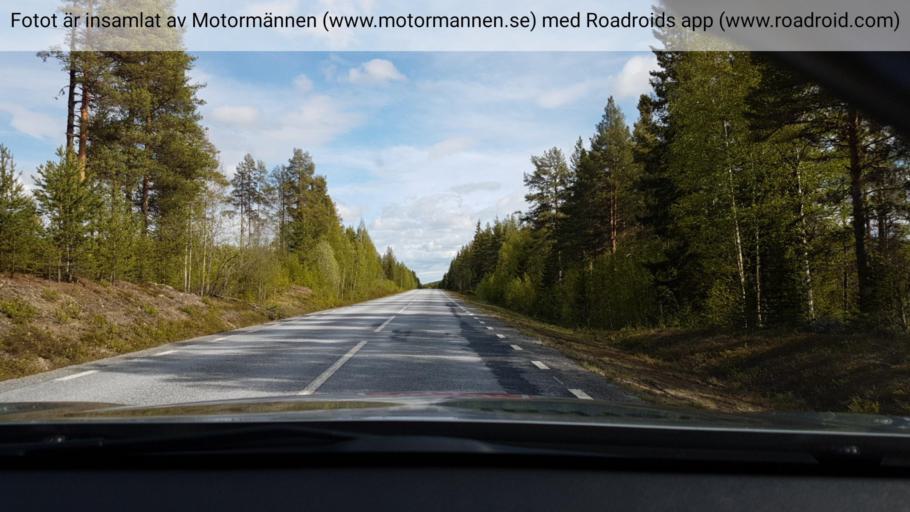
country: SE
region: Vaesterbotten
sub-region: Bjurholms Kommun
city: Bjurholm
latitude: 64.0226
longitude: 18.6685
